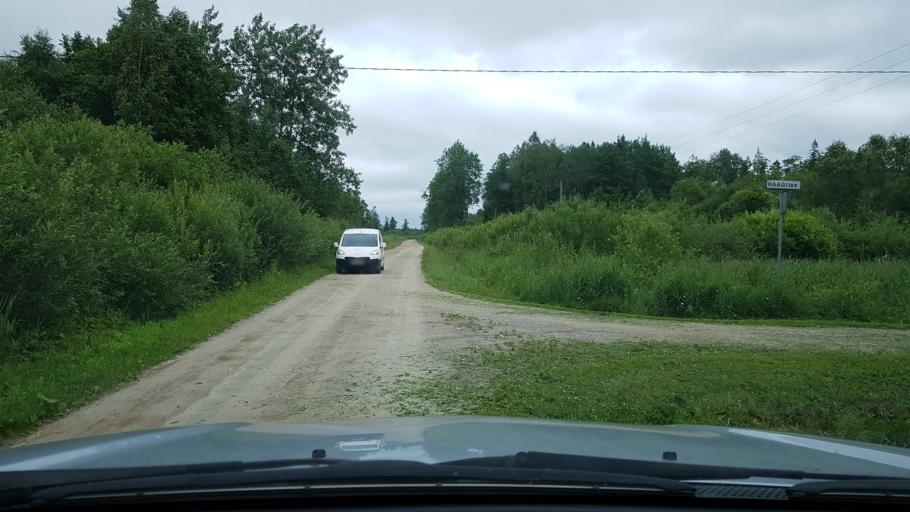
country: EE
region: Ida-Virumaa
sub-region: Narva-Joesuu linn
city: Narva-Joesuu
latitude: 59.3727
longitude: 28.0251
